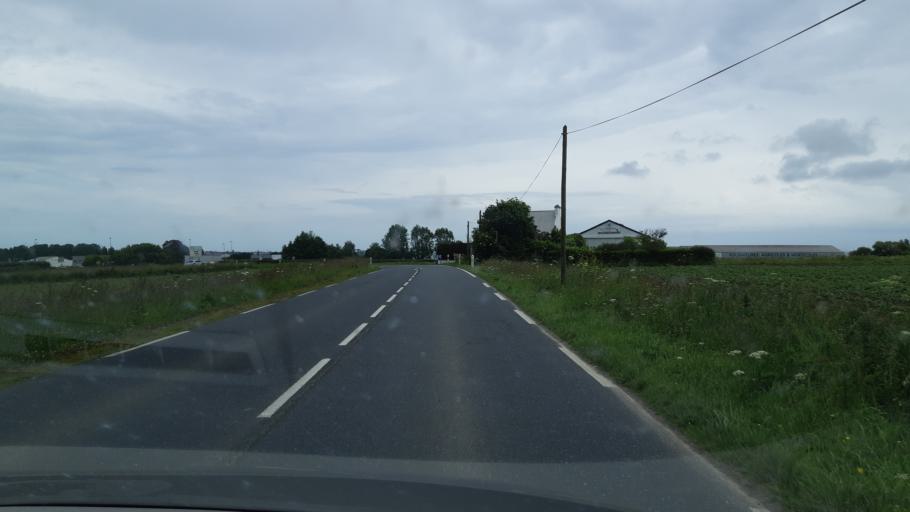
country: FR
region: Brittany
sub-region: Departement du Finistere
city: Saint-Pol-de-Leon
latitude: 48.6684
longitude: -4.0103
